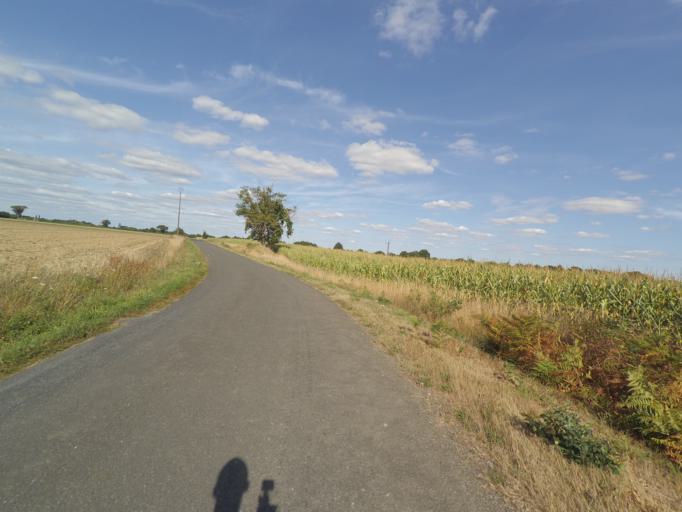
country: FR
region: Pays de la Loire
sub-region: Departement de la Loire-Atlantique
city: Vieillevigne
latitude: 46.9553
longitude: -1.4497
